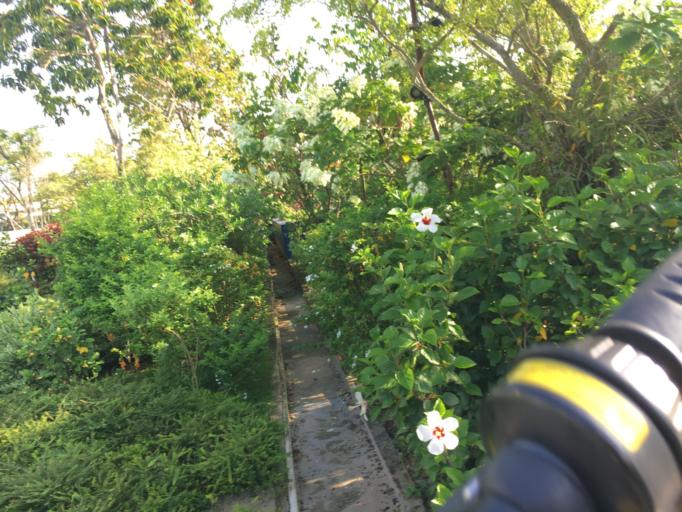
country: SG
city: Singapore
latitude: 1.2807
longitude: 103.8614
